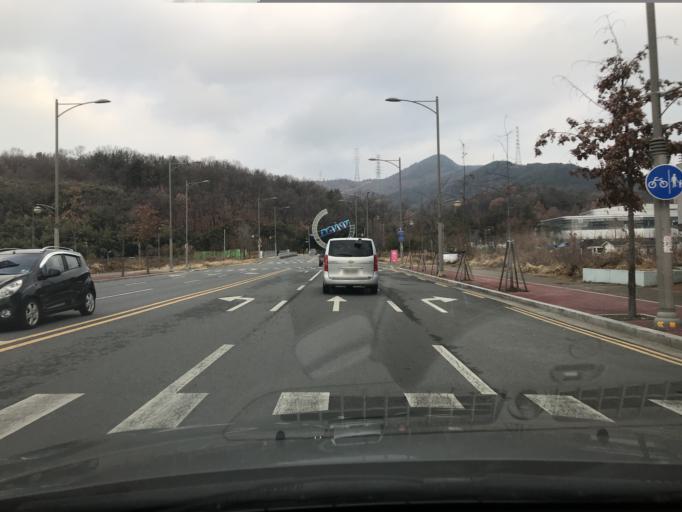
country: KR
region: Daegu
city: Hwawon
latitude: 35.6986
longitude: 128.4578
